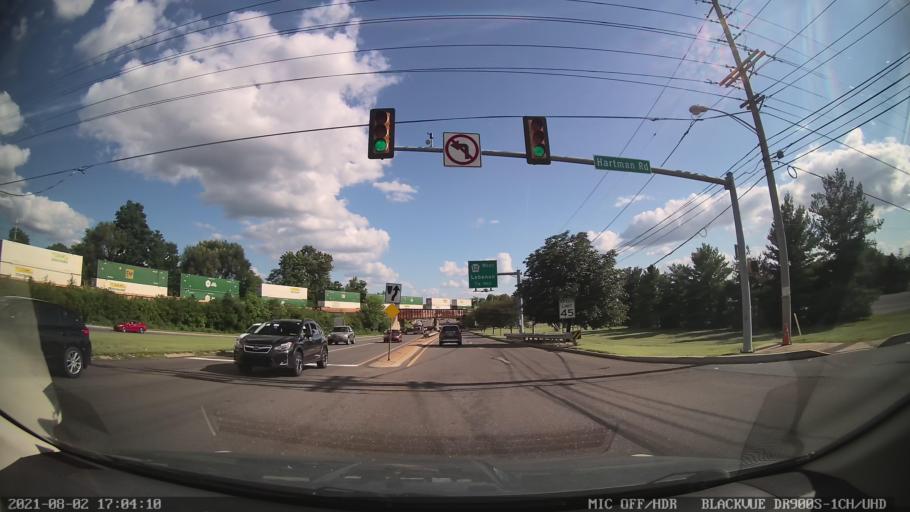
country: US
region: Pennsylvania
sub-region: Berks County
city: Hyde Park
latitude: 40.3745
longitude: -75.9334
